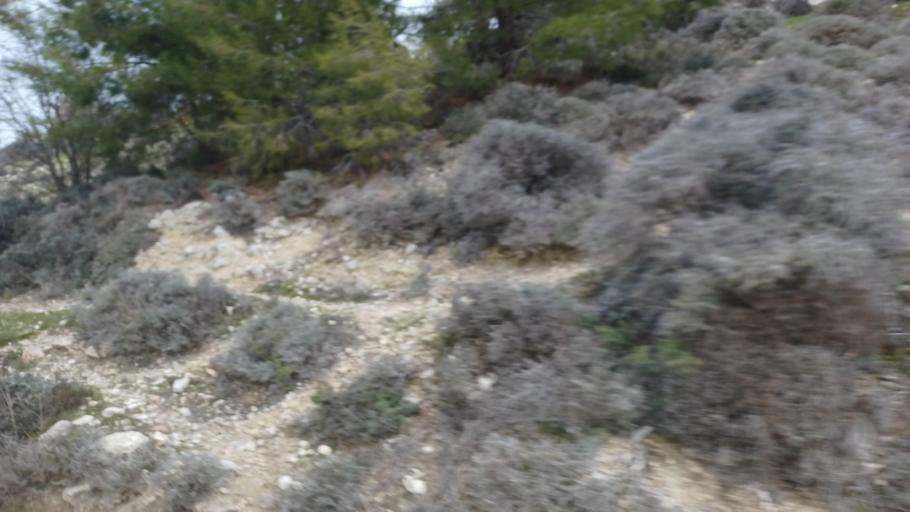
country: CY
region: Limassol
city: Pachna
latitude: 34.8430
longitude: 32.6772
